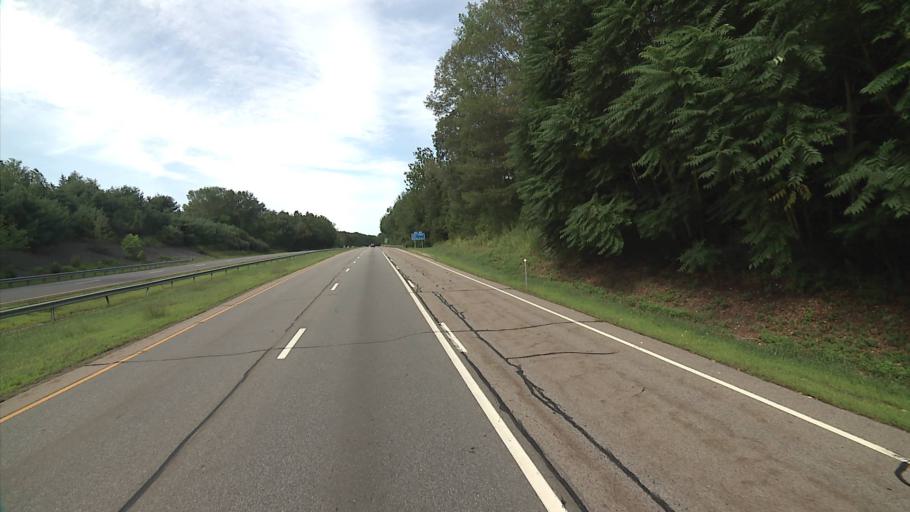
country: US
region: Connecticut
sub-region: New London County
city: Norwich
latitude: 41.5639
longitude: -72.1478
